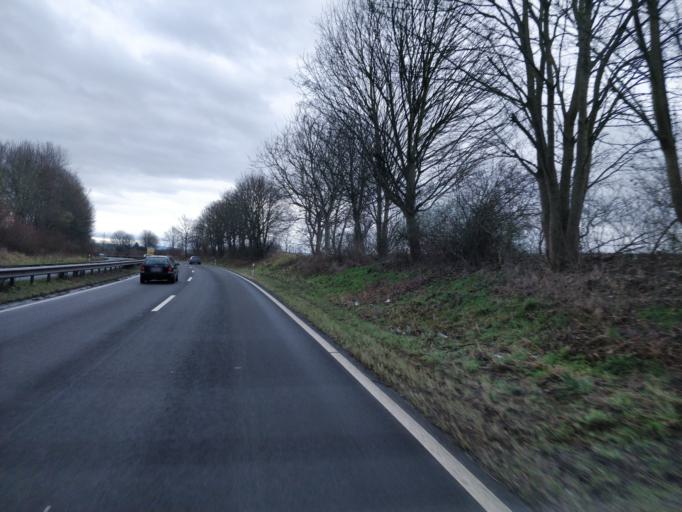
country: DE
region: Rheinland-Pfalz
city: Melsbach
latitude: 50.4584
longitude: 7.4808
